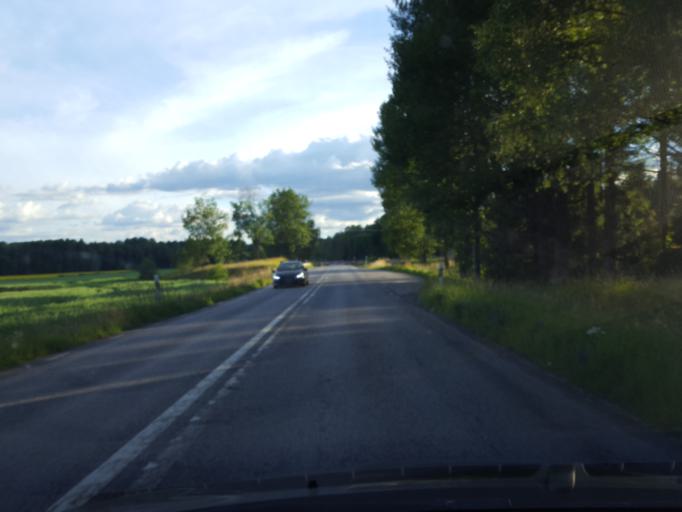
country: SE
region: Uppsala
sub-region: Osthammars Kommun
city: Gimo
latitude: 60.1190
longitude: 18.1443
